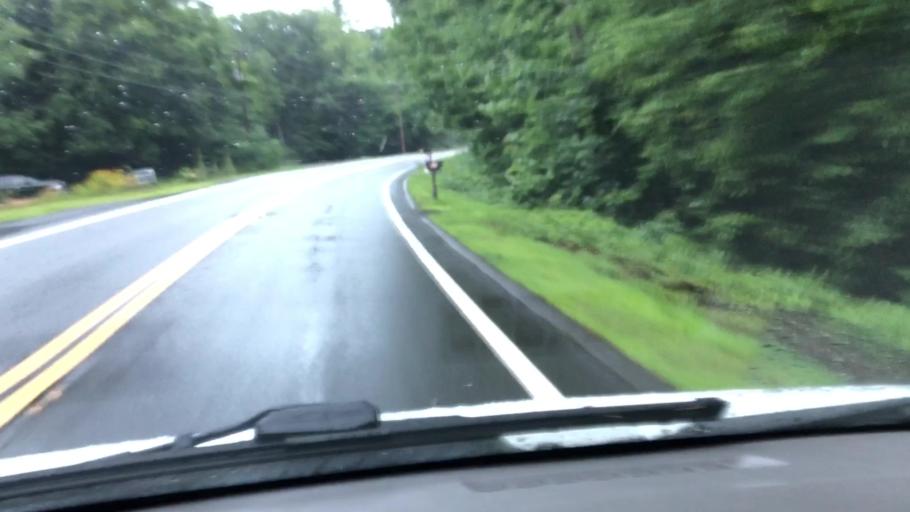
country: US
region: Massachusetts
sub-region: Hampshire County
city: Westhampton
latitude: 42.2793
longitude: -72.8661
